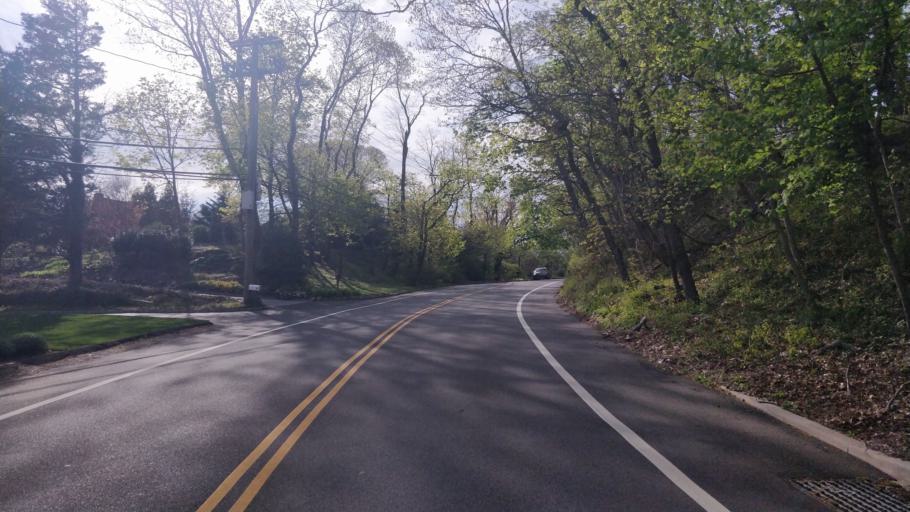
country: US
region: New York
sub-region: Suffolk County
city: East Setauket
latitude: 40.9451
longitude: -73.1172
